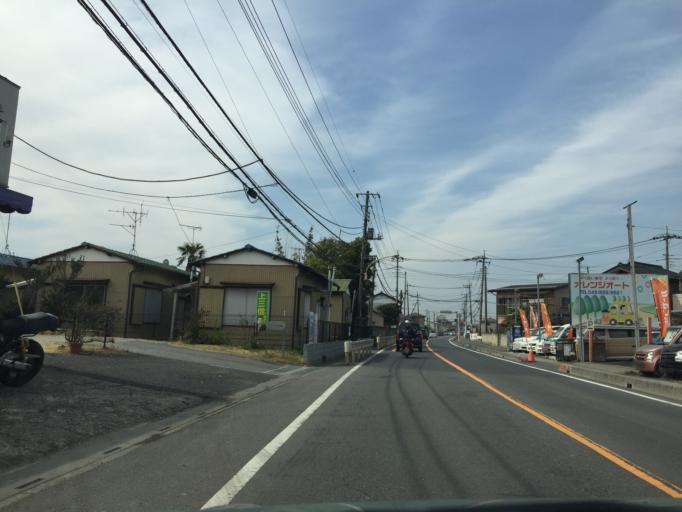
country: JP
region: Saitama
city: Yono
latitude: 35.8842
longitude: 139.5957
